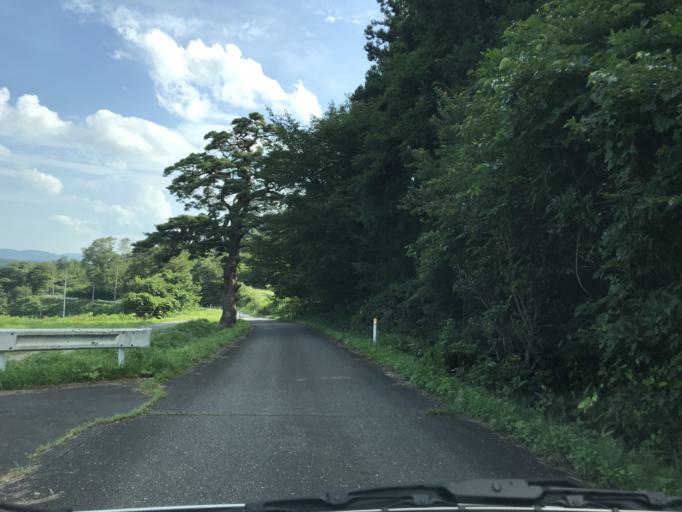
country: JP
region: Iwate
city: Ofunato
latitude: 38.9715
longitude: 141.4697
